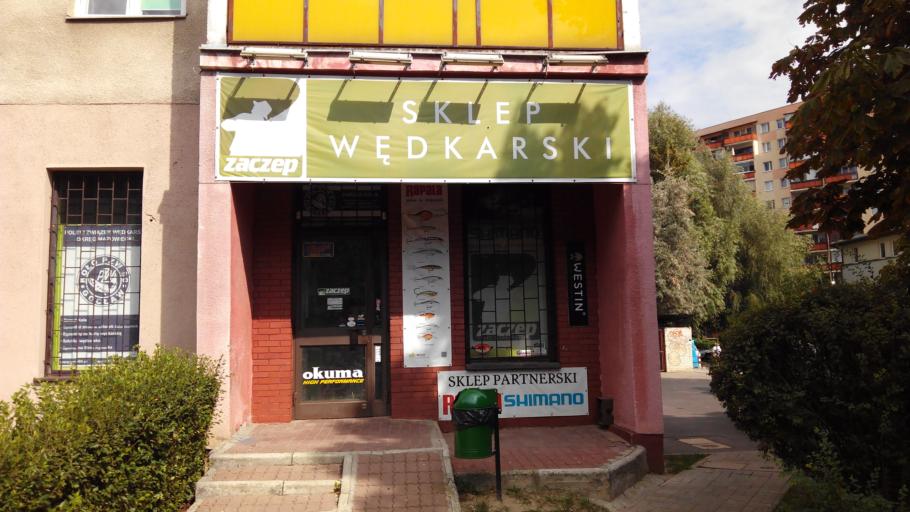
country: PL
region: Masovian Voivodeship
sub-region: Warszawa
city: Praga Poludnie
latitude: 52.2252
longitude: 21.0942
